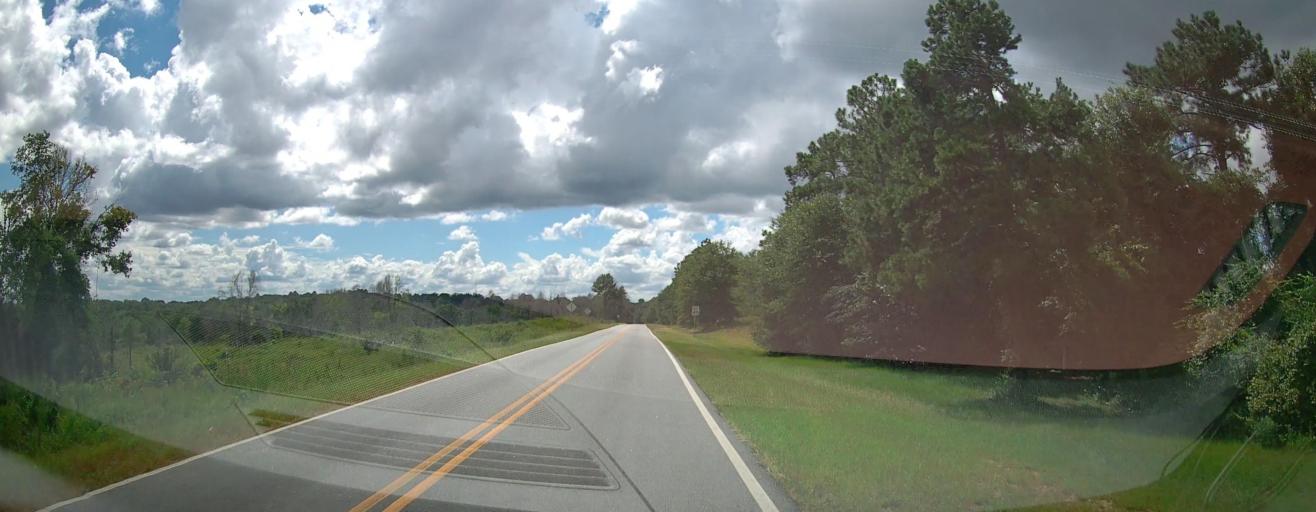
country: US
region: Georgia
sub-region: Chattahoochee County
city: Cusseta
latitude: 32.3072
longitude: -84.7604
